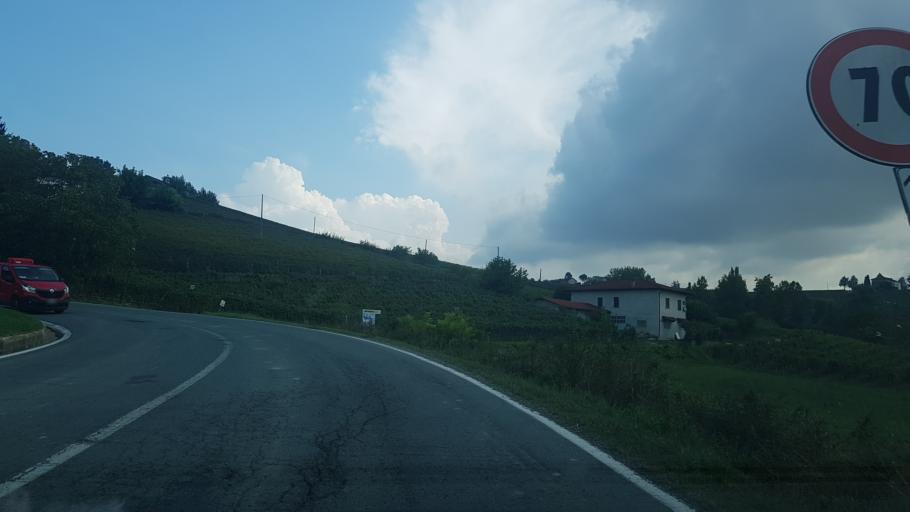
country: IT
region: Piedmont
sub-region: Provincia di Asti
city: Castelnuovo Belbo
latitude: 44.7774
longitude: 8.3917
